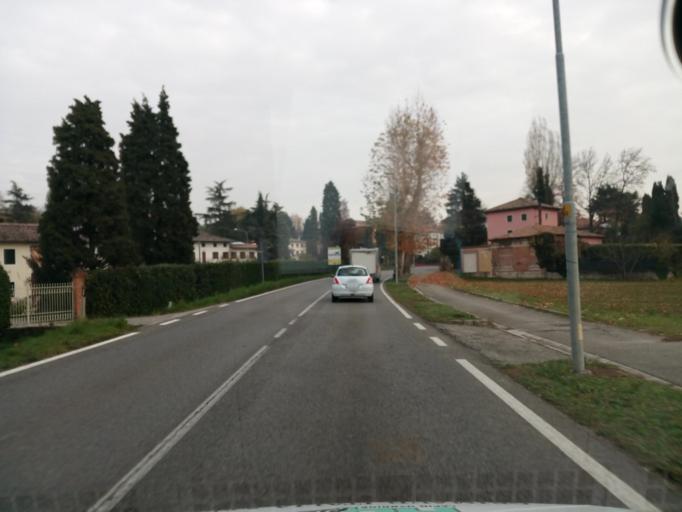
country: IT
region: Veneto
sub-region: Provincia di Treviso
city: One
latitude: 45.7819
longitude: 11.8606
